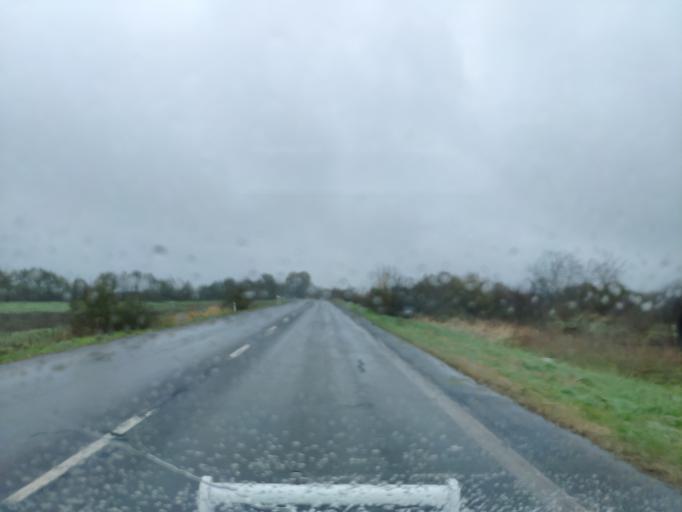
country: SK
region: Kosicky
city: Cierna nad Tisou
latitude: 48.4277
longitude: 21.9920
